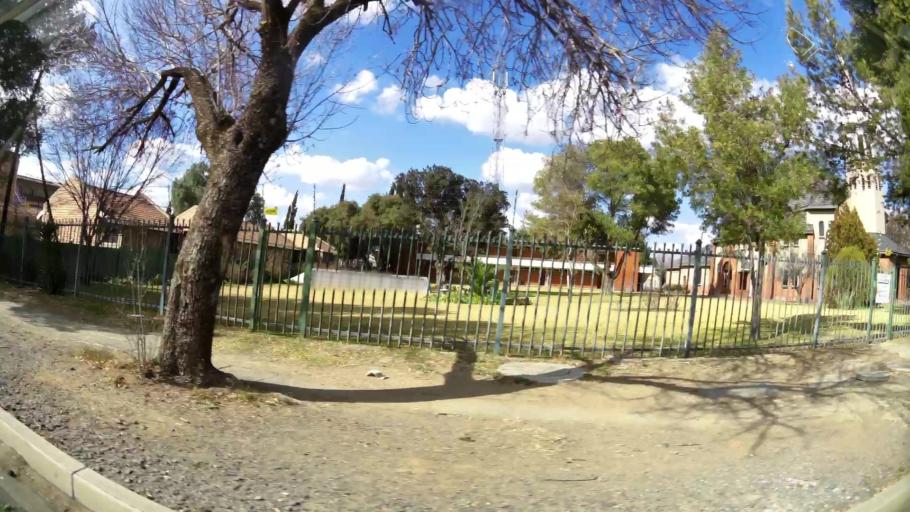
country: ZA
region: Orange Free State
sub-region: Mangaung Metropolitan Municipality
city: Bloemfontein
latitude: -29.1222
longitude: 26.1985
